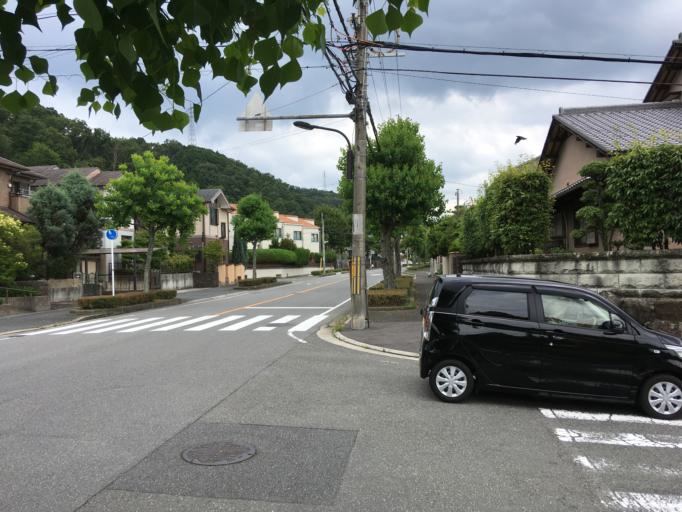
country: JP
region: Nara
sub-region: Ikoma-shi
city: Ikoma
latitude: 34.6797
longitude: 135.7181
